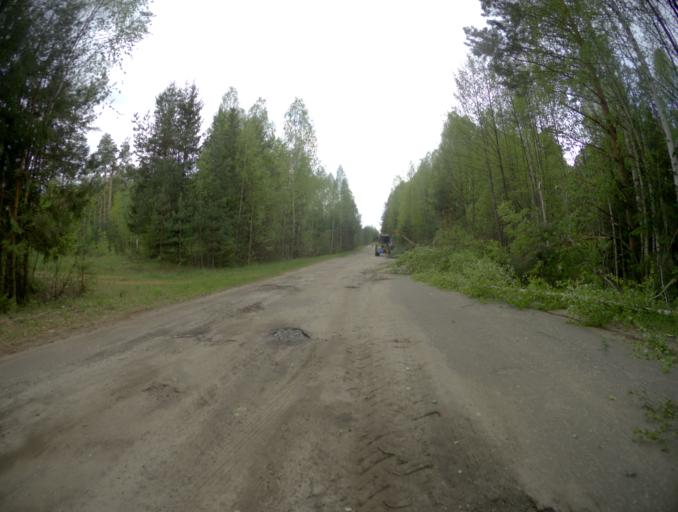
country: RU
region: Vladimir
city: Velikodvorskiy
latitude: 55.2451
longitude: 40.7085
